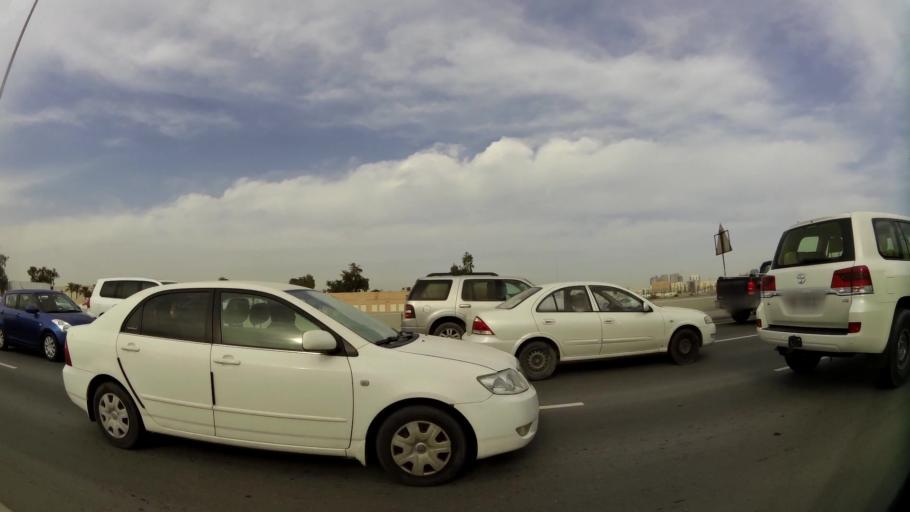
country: QA
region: Baladiyat ad Dawhah
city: Doha
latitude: 25.2849
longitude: 51.4826
